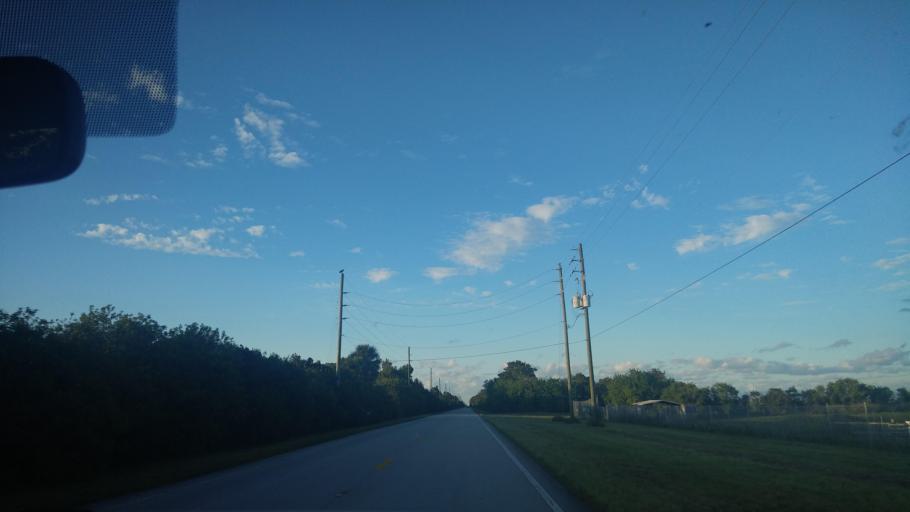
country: US
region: Florida
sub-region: Indian River County
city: Fellsmere
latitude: 27.6467
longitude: -80.6428
